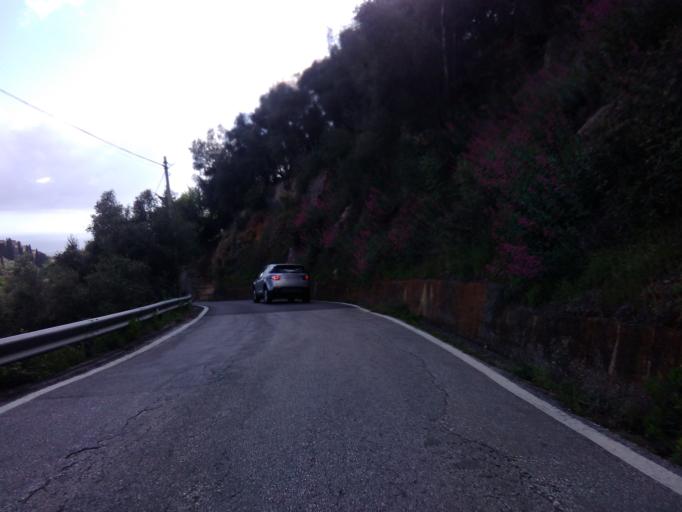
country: IT
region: Tuscany
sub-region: Provincia di Lucca
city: Piano di Mommio
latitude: 43.9519
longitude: 10.2723
